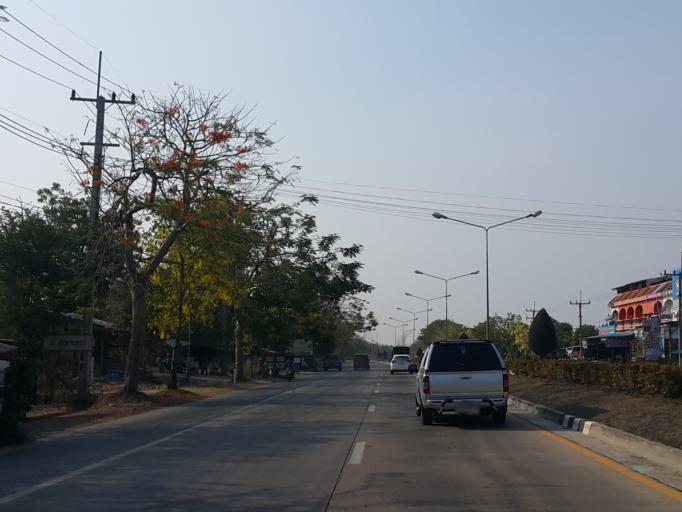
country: TH
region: Suphan Buri
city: Sam Chuk
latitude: 14.7613
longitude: 100.0947
